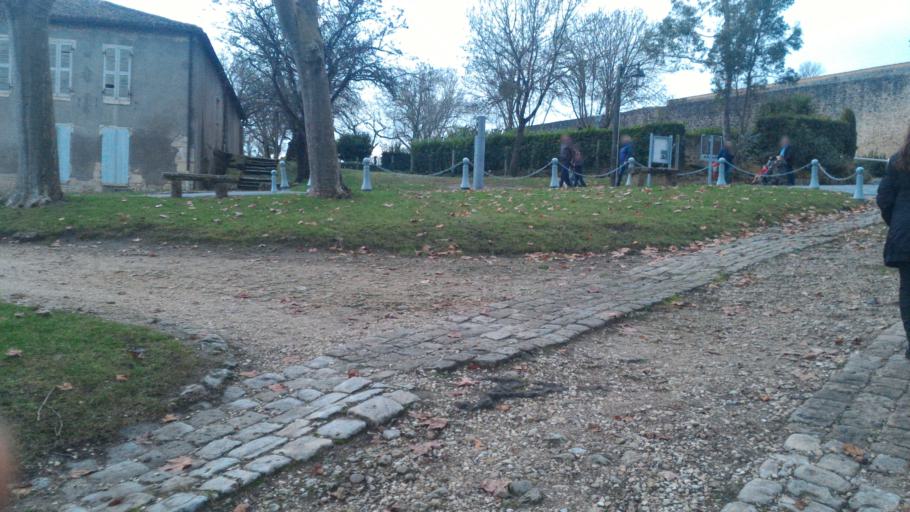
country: FR
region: Aquitaine
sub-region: Departement de la Gironde
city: Blaye
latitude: 45.1291
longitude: -0.6658
